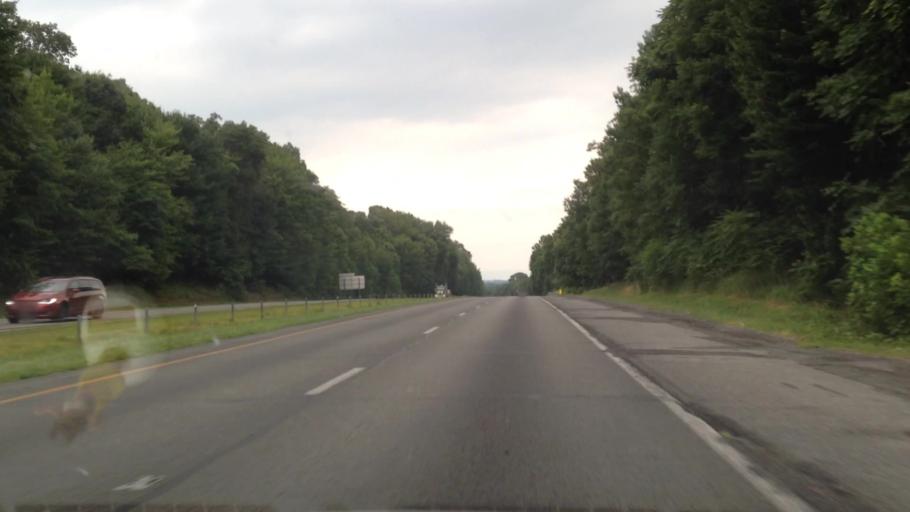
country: US
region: North Carolina
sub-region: Surry County
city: Pilot Mountain
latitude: 36.3493
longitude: -80.4659
